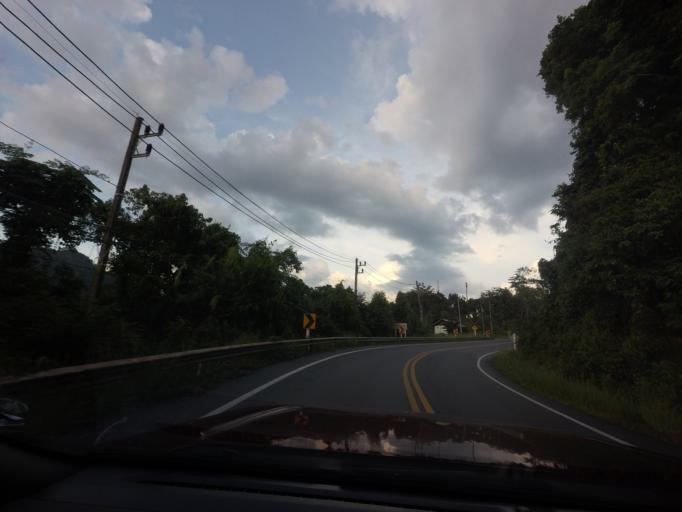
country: TH
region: Yala
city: Than To
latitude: 6.0467
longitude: 101.1990
